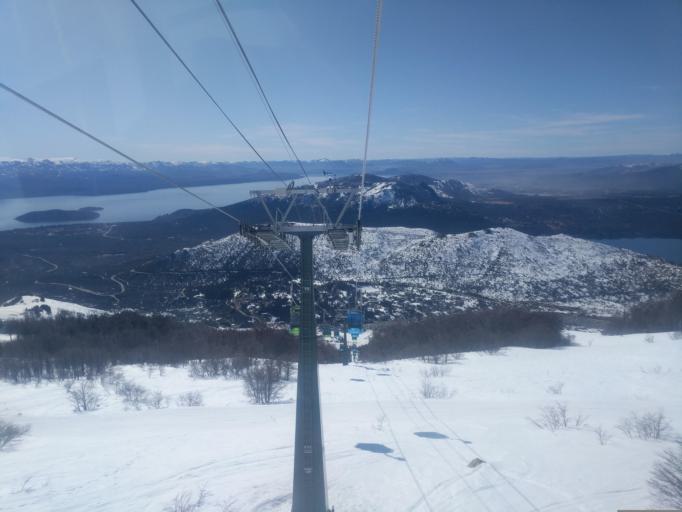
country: AR
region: Rio Negro
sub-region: Departamento de Bariloche
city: San Carlos de Bariloche
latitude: -41.1752
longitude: -71.4624
